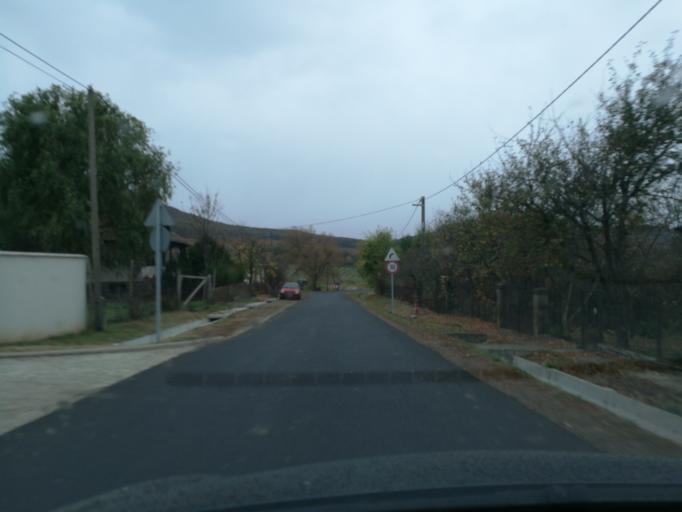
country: HU
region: Nograd
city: Paszto
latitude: 47.9775
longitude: 19.6388
